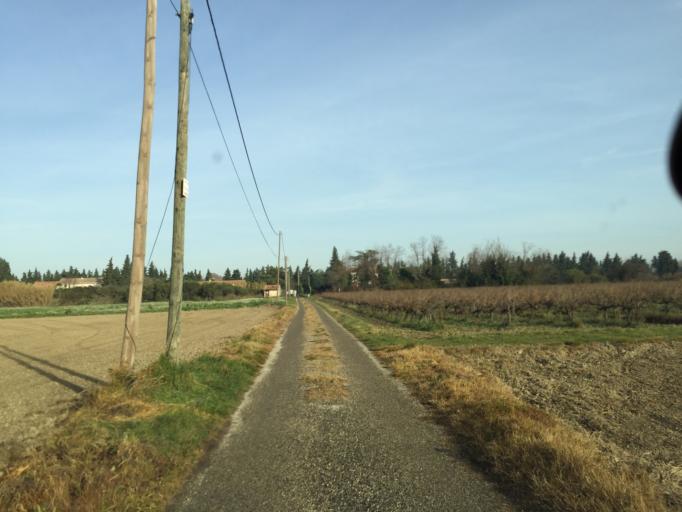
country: FR
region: Provence-Alpes-Cote d'Azur
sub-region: Departement du Vaucluse
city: Orange
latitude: 44.1536
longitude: 4.8061
